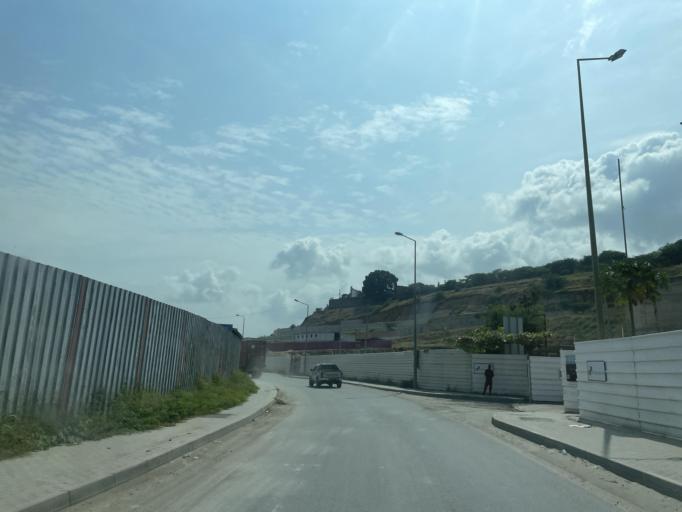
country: AO
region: Luanda
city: Luanda
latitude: -8.8063
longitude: 13.2453
